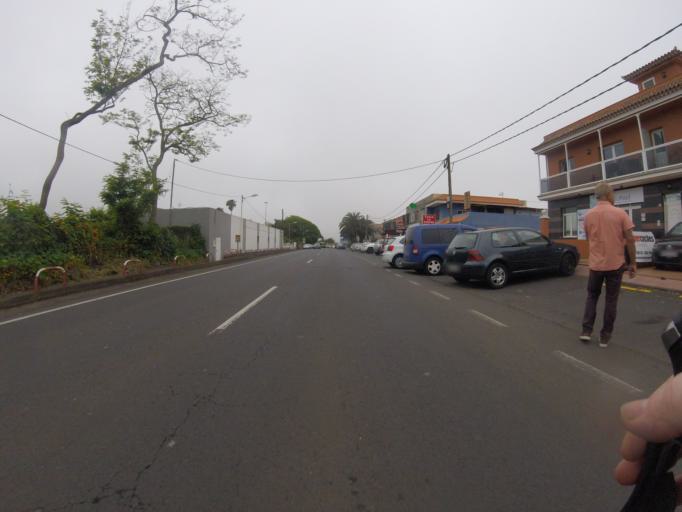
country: ES
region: Canary Islands
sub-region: Provincia de Santa Cruz de Tenerife
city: Tacoronte
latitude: 28.4923
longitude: -16.3679
